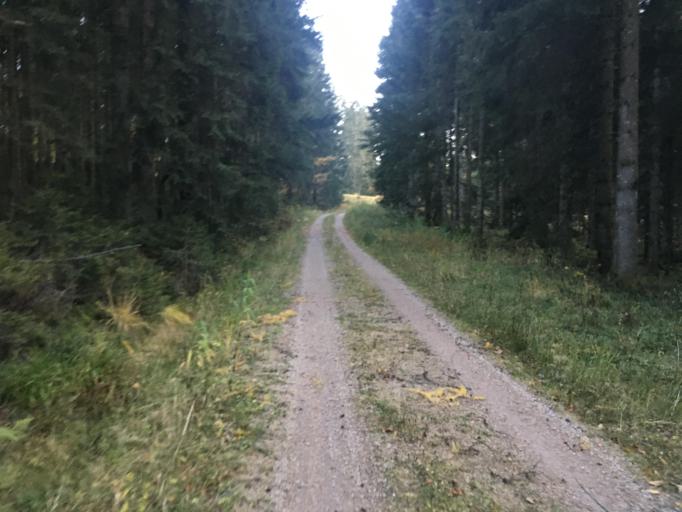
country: DE
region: Baden-Wuerttemberg
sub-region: Freiburg Region
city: Bad Peterstal-Griesbach
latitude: 48.4956
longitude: 8.2495
